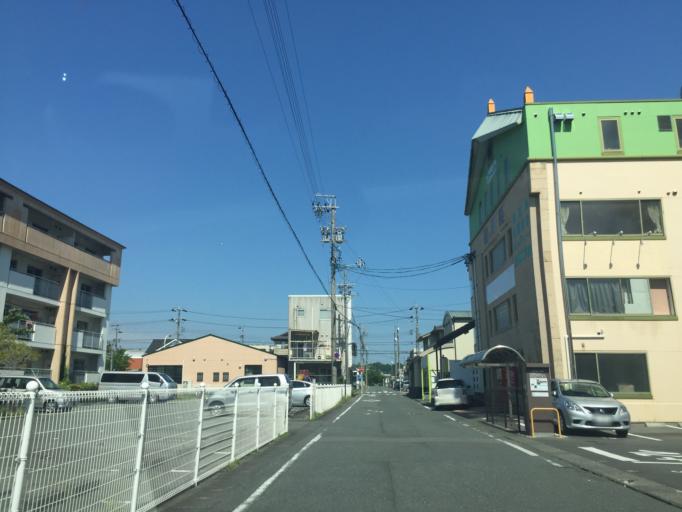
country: JP
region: Shizuoka
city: Kakegawa
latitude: 34.7734
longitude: 138.0176
